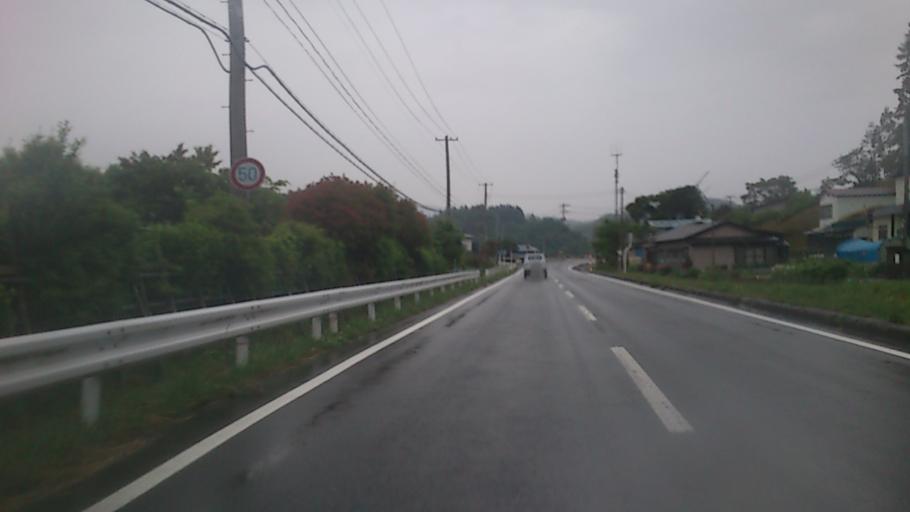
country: JP
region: Akita
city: Takanosu
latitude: 40.2879
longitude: 140.2666
